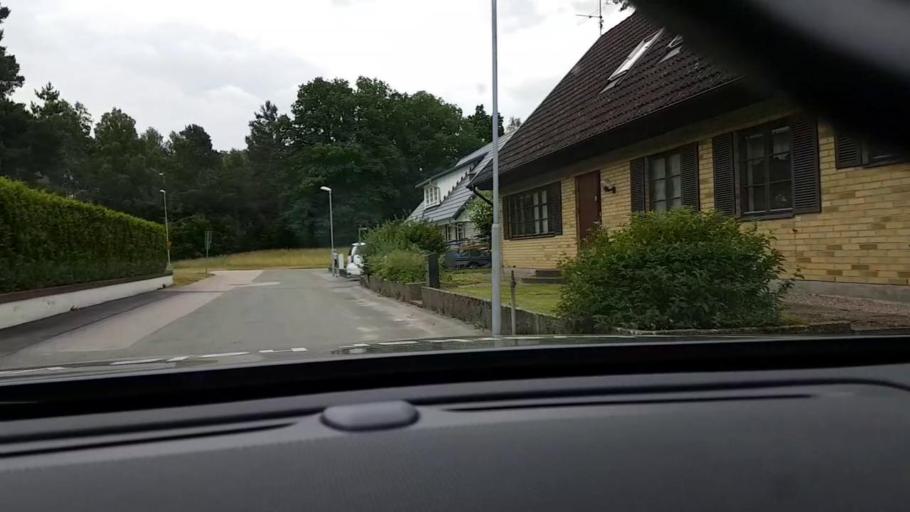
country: SE
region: Skane
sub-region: Hassleholms Kommun
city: Hassleholm
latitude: 56.1722
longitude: 13.8017
